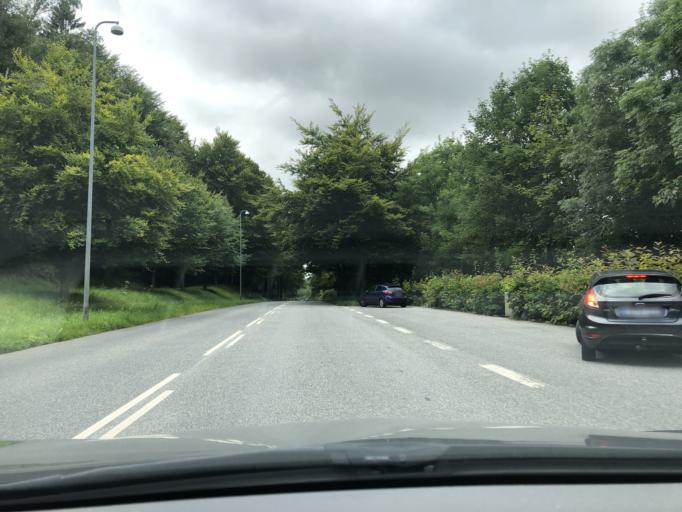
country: DK
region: South Denmark
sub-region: Vejle Kommune
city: Vejle
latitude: 55.6994
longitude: 9.5064
